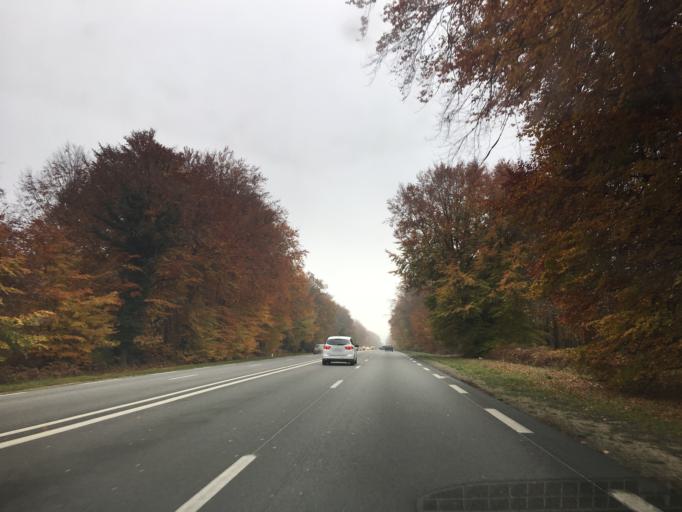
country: FR
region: Ile-de-France
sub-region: Departement de Seine-et-Marne
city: Fontainebleau
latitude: 48.4255
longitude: 2.6659
